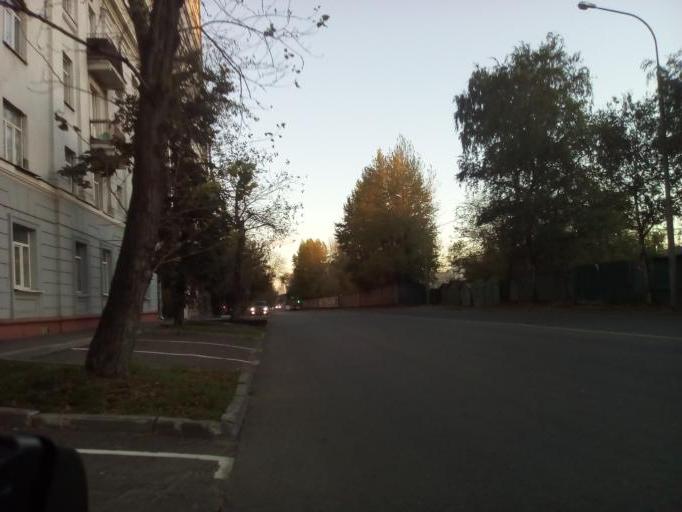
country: RU
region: Moscow
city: Sokol
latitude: 55.8056
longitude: 37.4943
